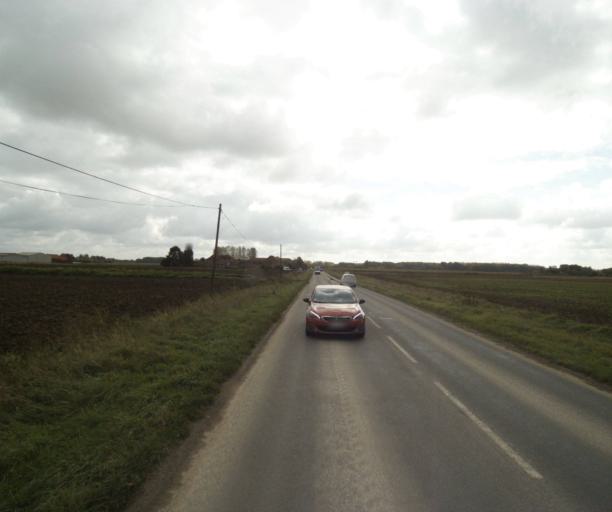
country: FR
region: Nord-Pas-de-Calais
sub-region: Departement du Nord
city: Verlinghem
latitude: 50.6950
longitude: 2.9801
